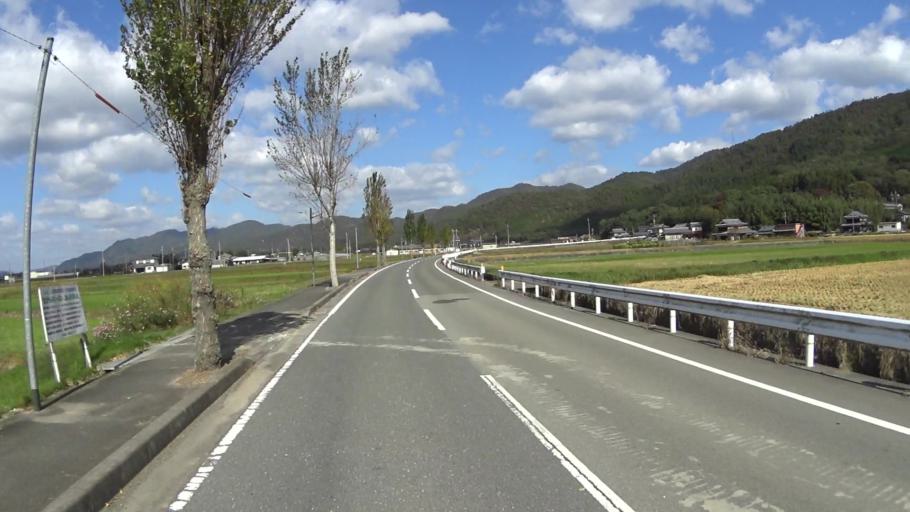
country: JP
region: Kyoto
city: Kameoka
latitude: 35.0719
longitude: 135.5660
